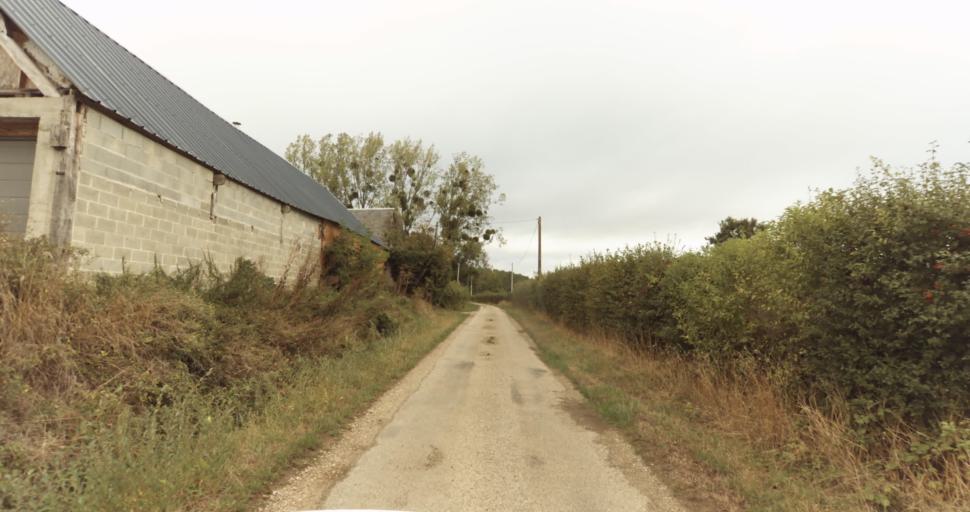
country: FR
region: Lower Normandy
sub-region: Departement de l'Orne
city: Trun
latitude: 48.9194
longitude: 0.0832
